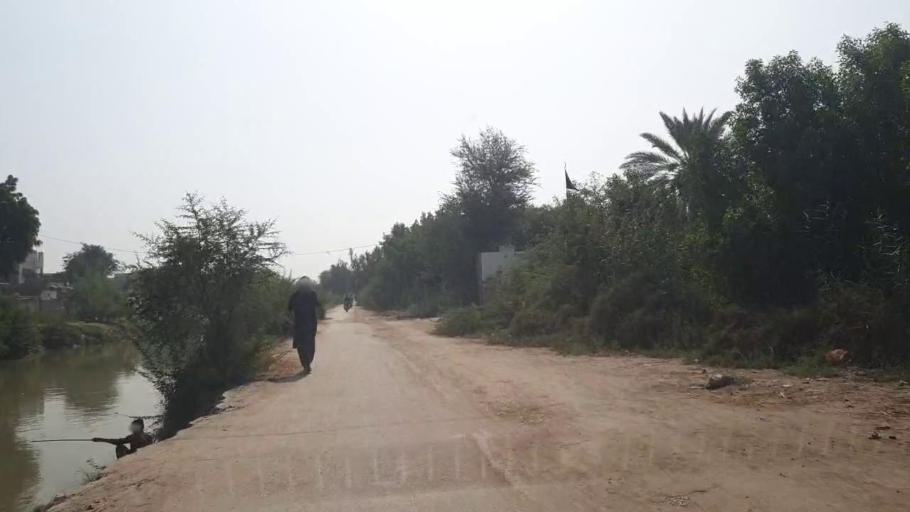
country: PK
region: Sindh
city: Badin
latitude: 24.6536
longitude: 68.8429
